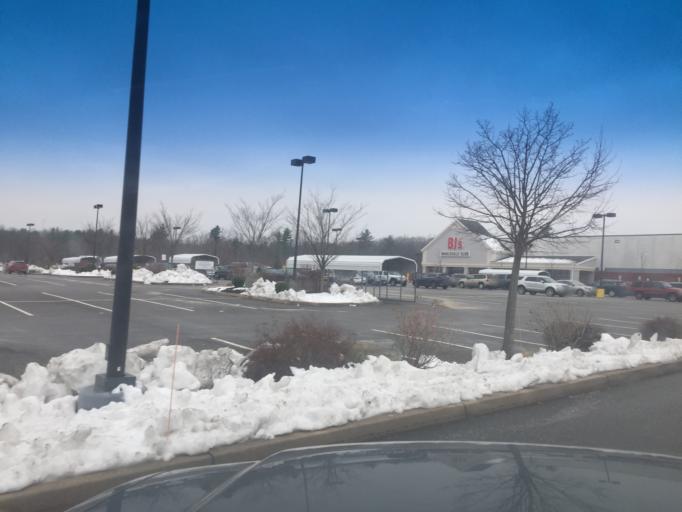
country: US
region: Massachusetts
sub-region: Middlesex County
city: Hudson
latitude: 42.3960
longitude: -71.5994
